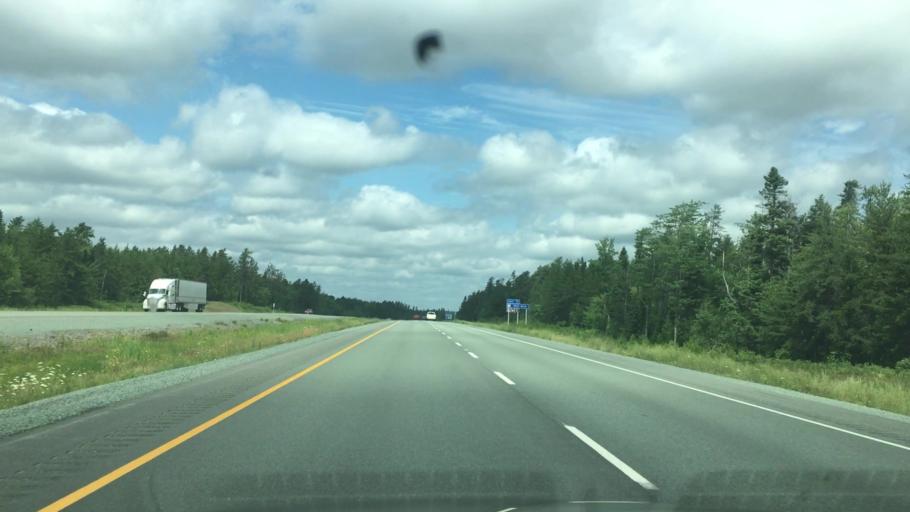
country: CA
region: Nova Scotia
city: Oxford
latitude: 45.6678
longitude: -63.7503
